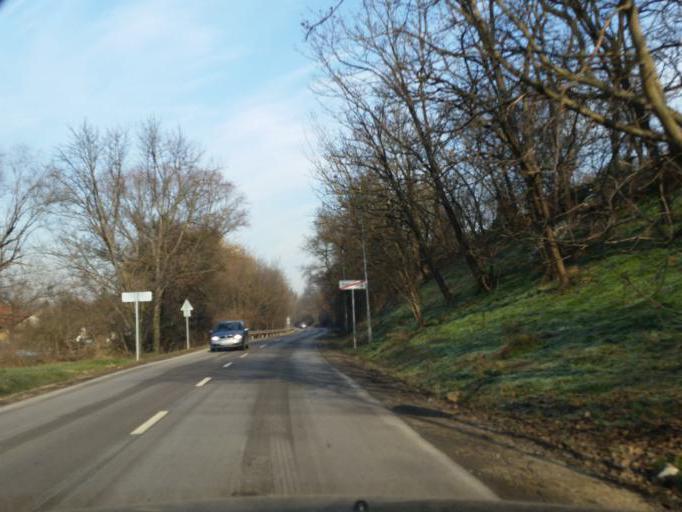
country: HU
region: Pest
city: Biatorbagy
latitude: 47.4808
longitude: 18.8285
